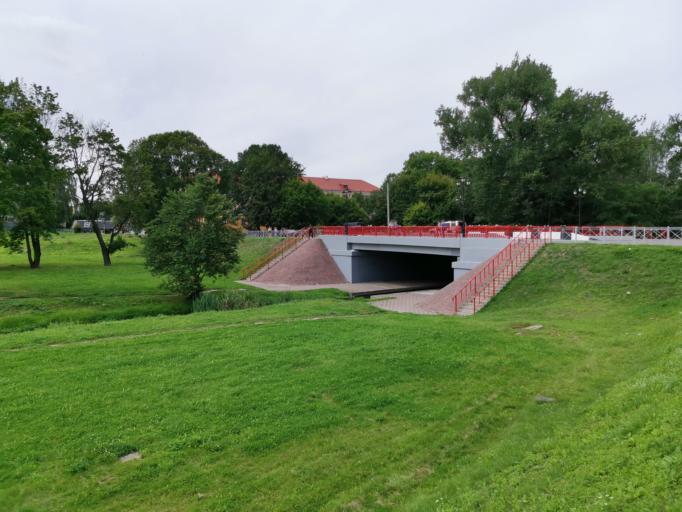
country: RU
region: Kaliningrad
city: Chernyakhovsk
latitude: 54.6357
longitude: 21.8052
